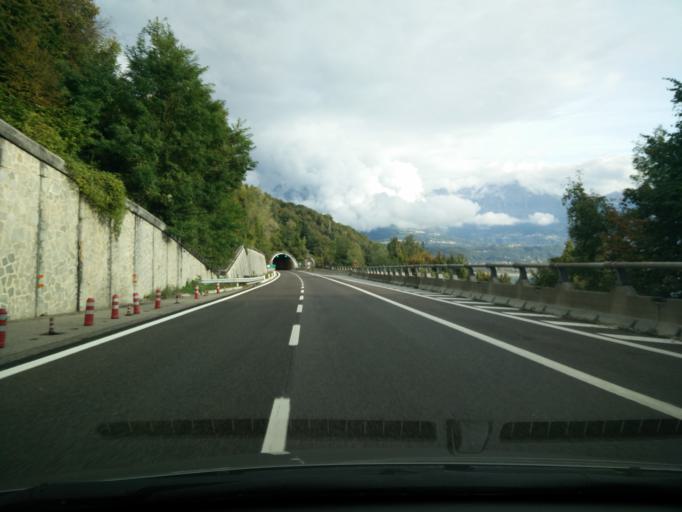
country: IT
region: Veneto
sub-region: Provincia di Belluno
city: Farra d'Alpago
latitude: 46.0987
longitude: 12.3247
